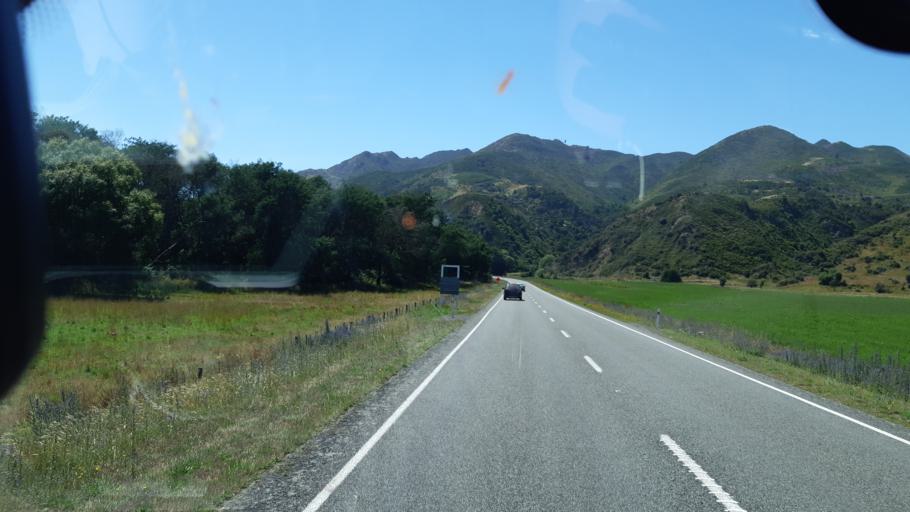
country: NZ
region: Canterbury
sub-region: Kaikoura District
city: Kaikoura
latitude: -42.6368
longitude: 173.3370
